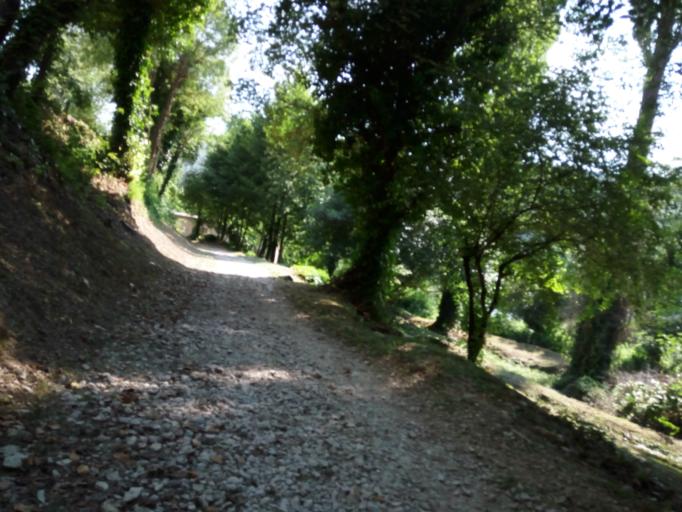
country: HR
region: Sibensko-Kniniska
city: Kistanje
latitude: 43.9032
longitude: 15.9770
